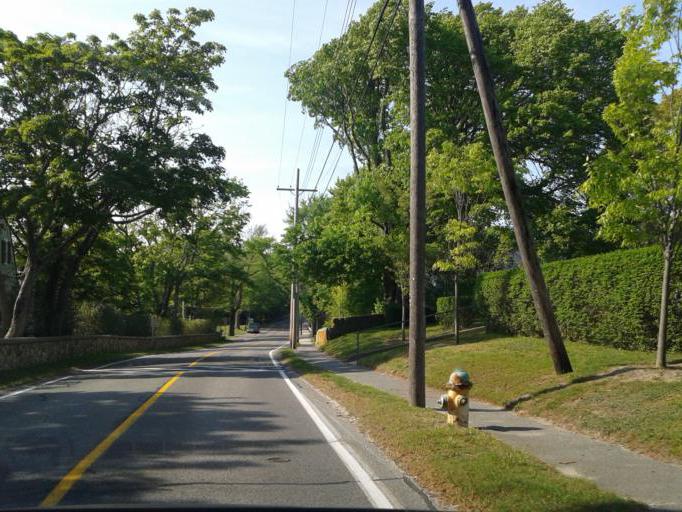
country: US
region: Massachusetts
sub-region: Barnstable County
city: Falmouth
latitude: 41.5213
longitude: -70.6630
